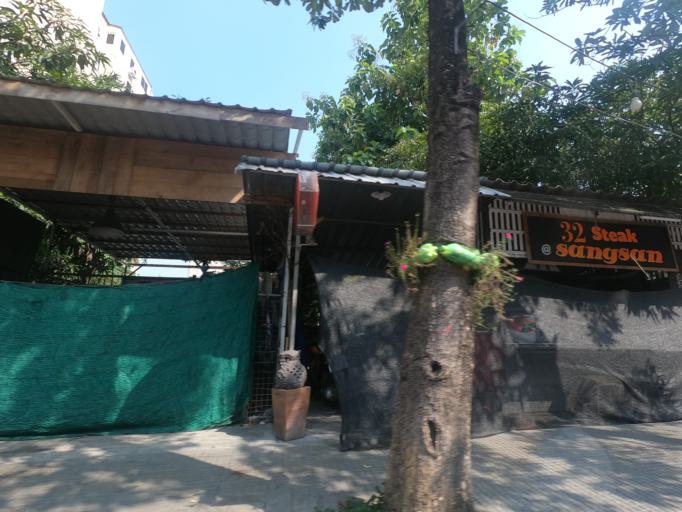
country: TH
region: Bangkok
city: Chatuchak
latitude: 13.8179
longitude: 100.5832
